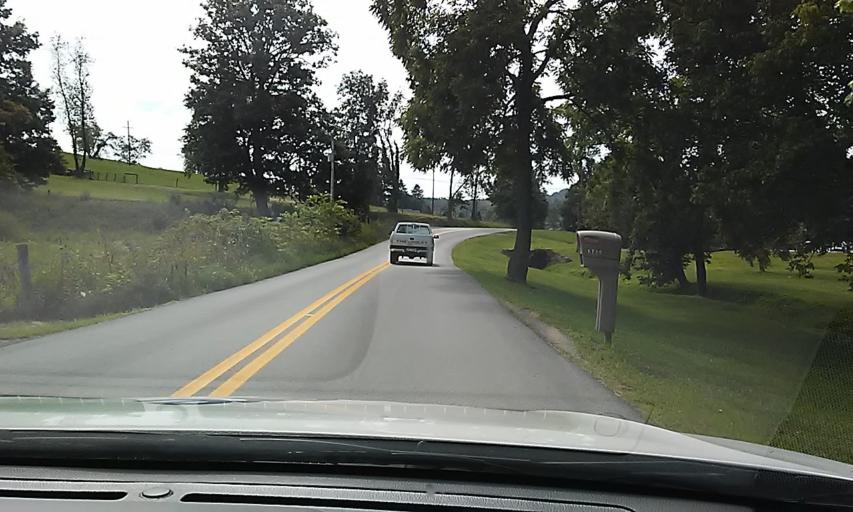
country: US
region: West Virginia
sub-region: Monongalia County
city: Star City
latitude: 39.6234
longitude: -80.0860
